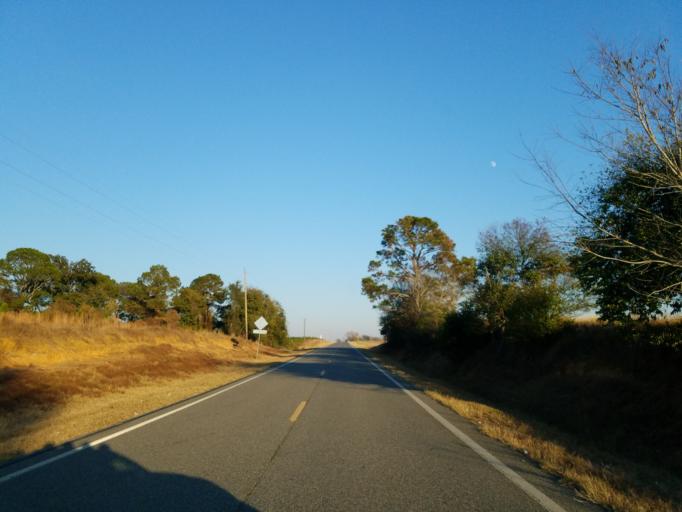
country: US
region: Georgia
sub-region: Turner County
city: Ashburn
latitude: 31.8596
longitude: -83.6118
